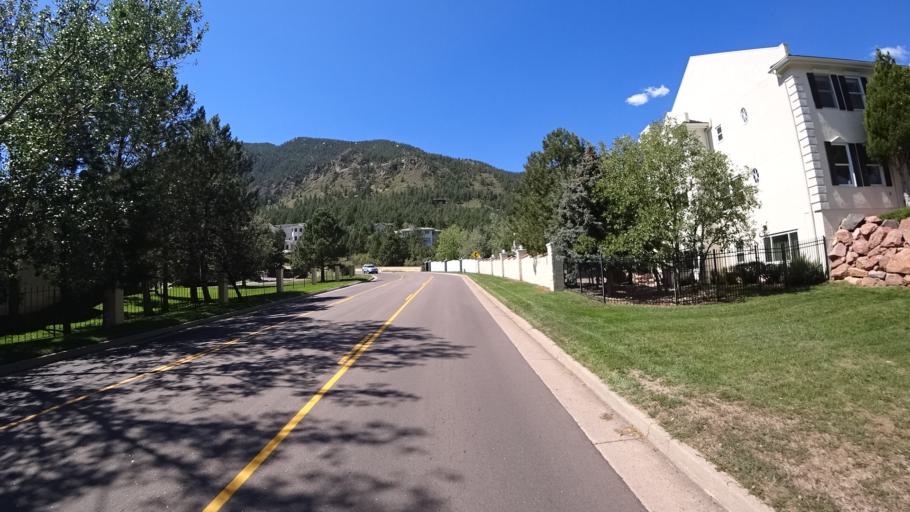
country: US
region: Colorado
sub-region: El Paso County
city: Colorado Springs
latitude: 38.7781
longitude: -104.8558
